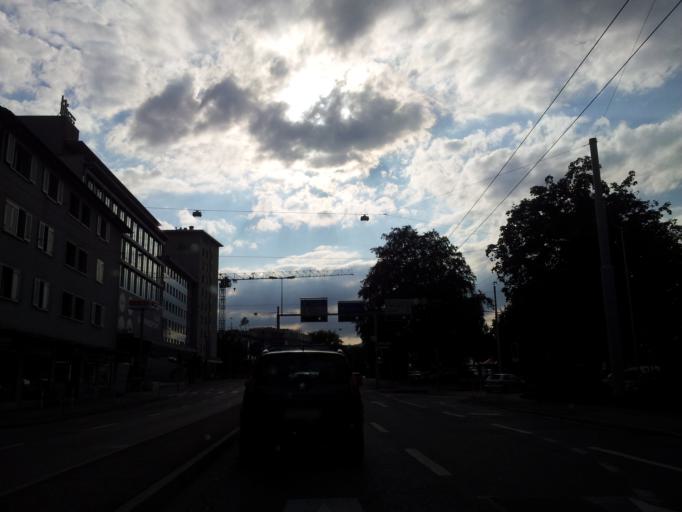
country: CH
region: Zurich
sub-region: Bezirk Dietikon
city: Schlieren / Zentrum
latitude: 47.3979
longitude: 8.4498
